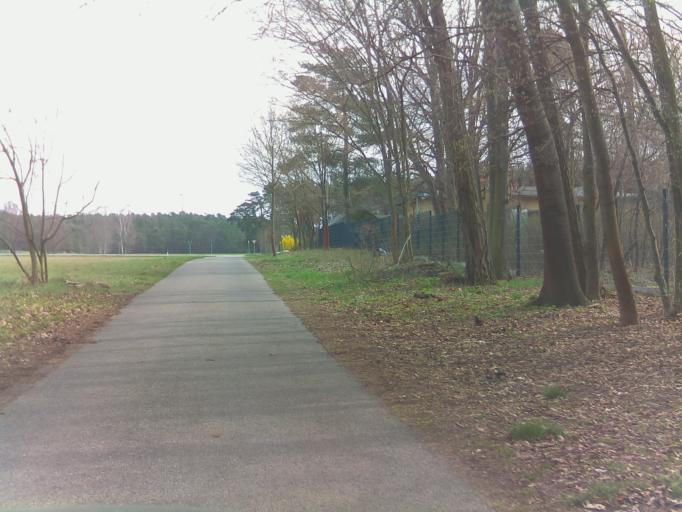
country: DE
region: Brandenburg
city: Vetschau
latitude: 51.7737
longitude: 14.0654
